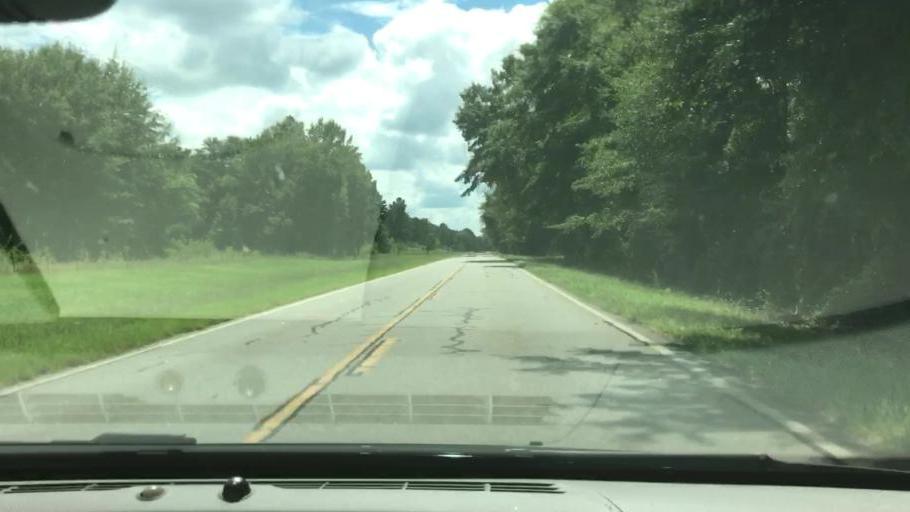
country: US
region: Georgia
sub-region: Quitman County
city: Georgetown
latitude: 32.1096
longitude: -85.0381
